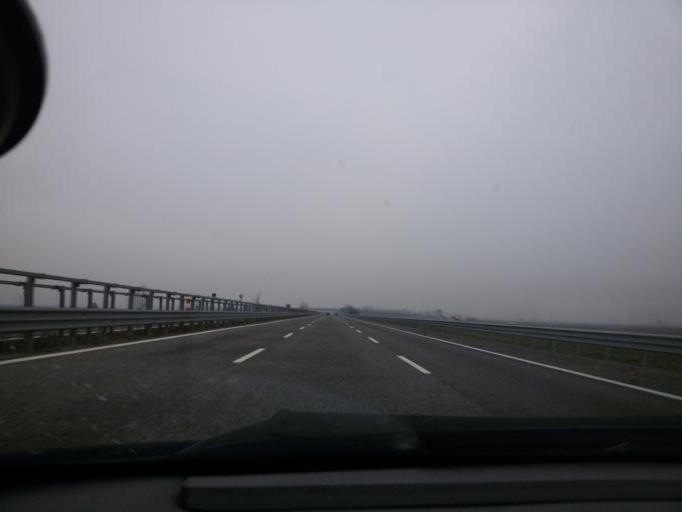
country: IT
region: Piedmont
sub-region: Provincia di Vercelli
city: Stroppiana
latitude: 45.2269
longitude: 8.4761
